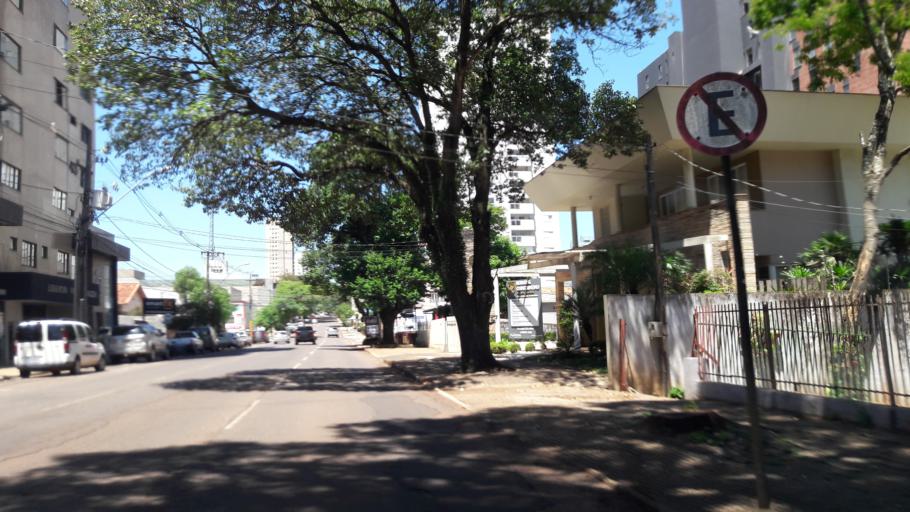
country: BR
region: Parana
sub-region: Cascavel
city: Cascavel
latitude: -24.9494
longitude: -53.4467
